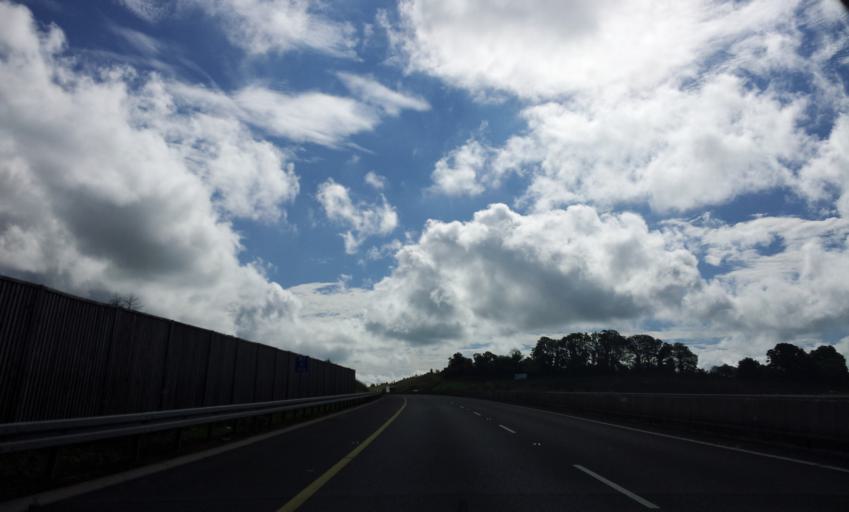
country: IE
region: Munster
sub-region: North Tipperary
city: Roscrea
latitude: 52.9185
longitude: -7.7203
